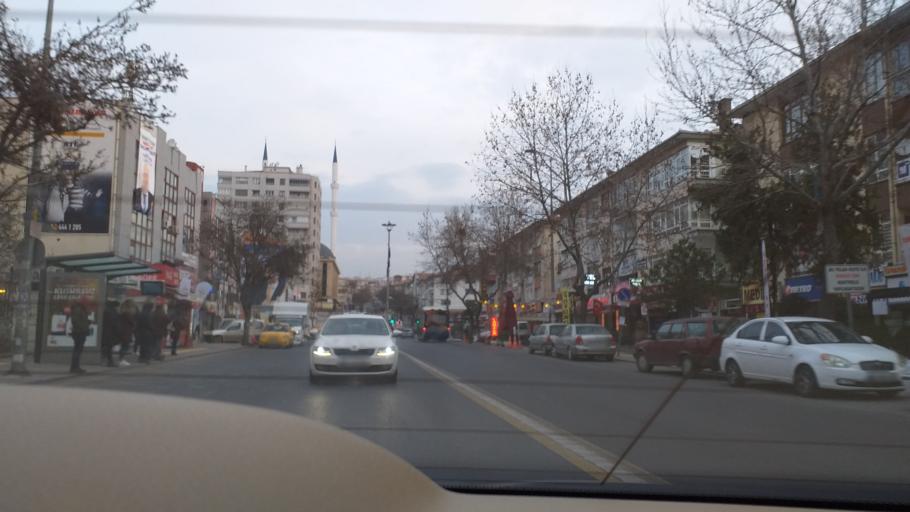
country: TR
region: Ankara
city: Ankara
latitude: 39.9716
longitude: 32.8429
